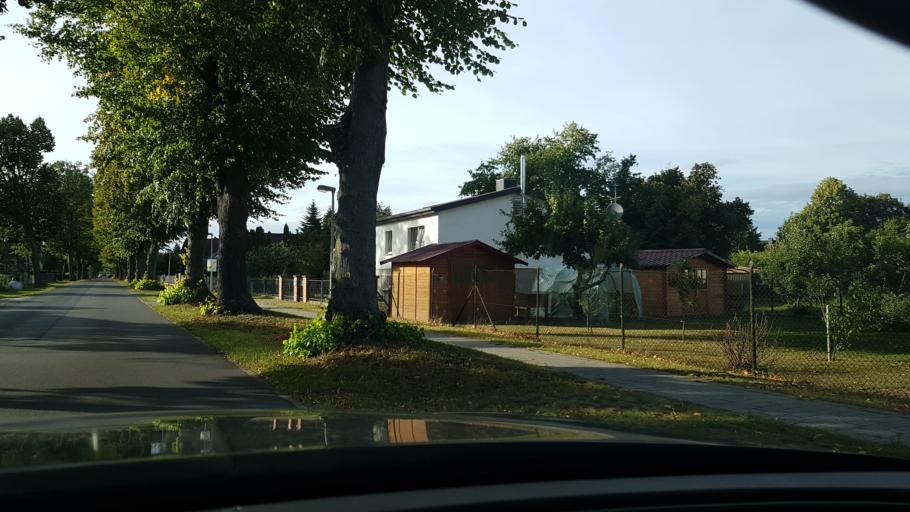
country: DE
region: Brandenburg
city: Brieselang
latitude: 52.5920
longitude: 12.9931
